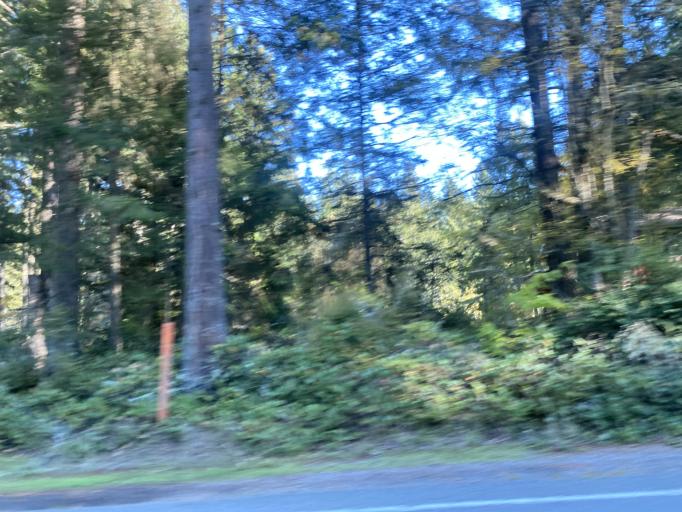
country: US
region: Washington
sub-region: Island County
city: Langley
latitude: 48.0118
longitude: -122.4262
